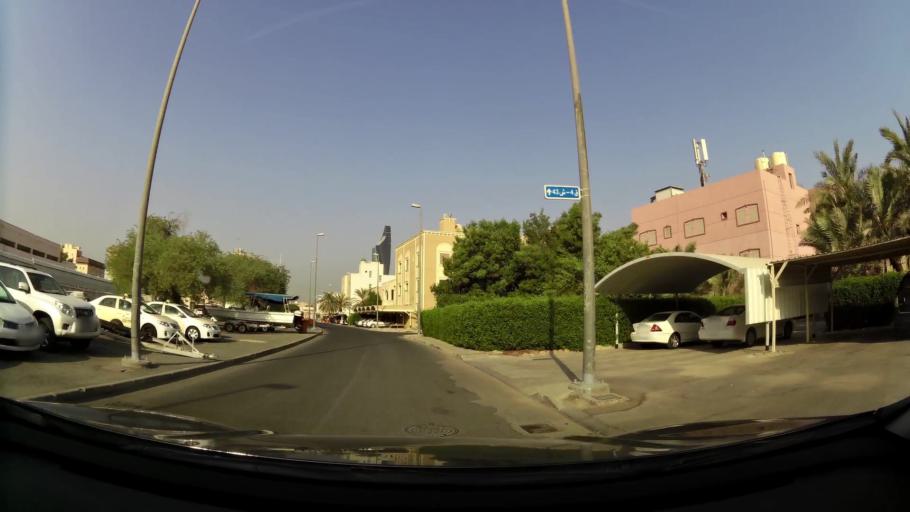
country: KW
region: Al Asimah
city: Ad Dasmah
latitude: 29.3680
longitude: 48.0029
